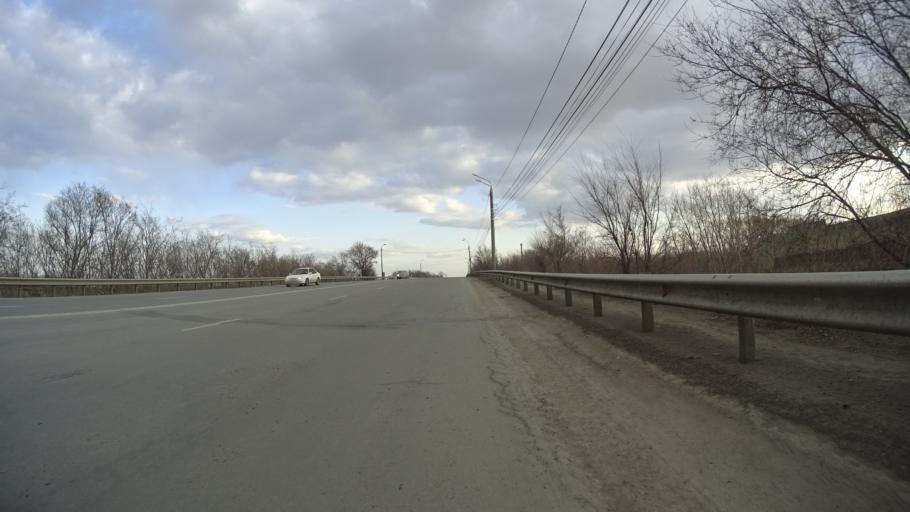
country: RU
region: Chelyabinsk
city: Novosineglazovskiy
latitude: 55.1033
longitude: 61.3874
